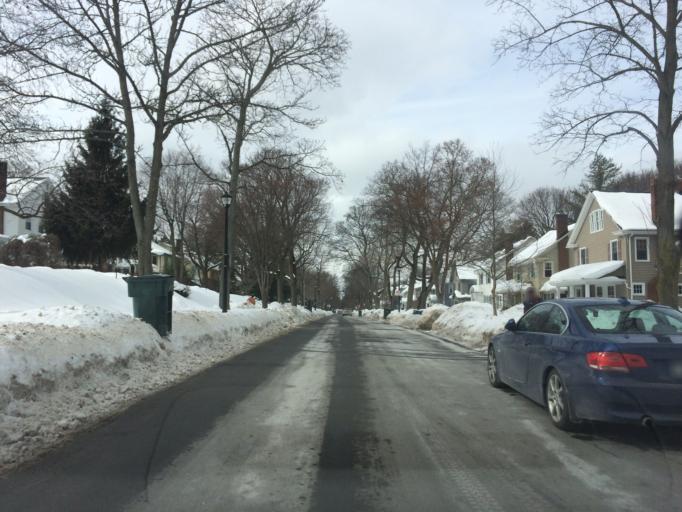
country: US
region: New York
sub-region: Monroe County
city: Rochester
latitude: 43.1347
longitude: -77.5998
